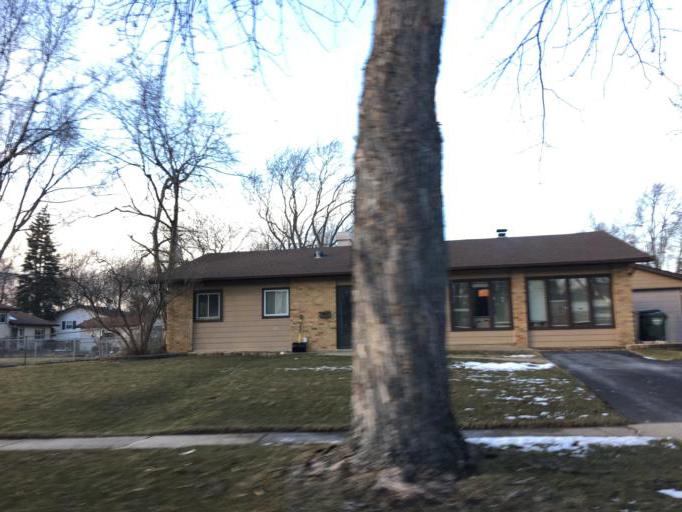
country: US
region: Illinois
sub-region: Cook County
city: Hoffman Estates
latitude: 42.0426
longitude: -88.0916
